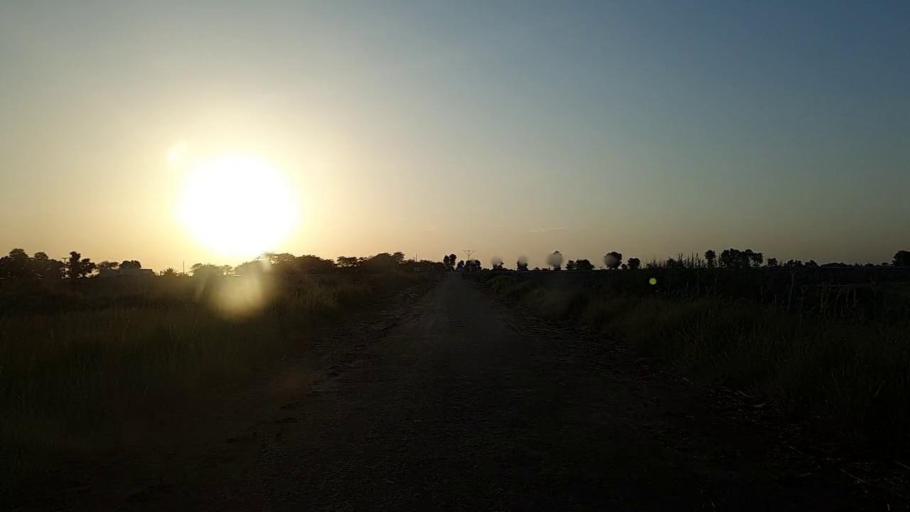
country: PK
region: Sindh
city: Hingorja
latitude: 27.0606
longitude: 68.3957
